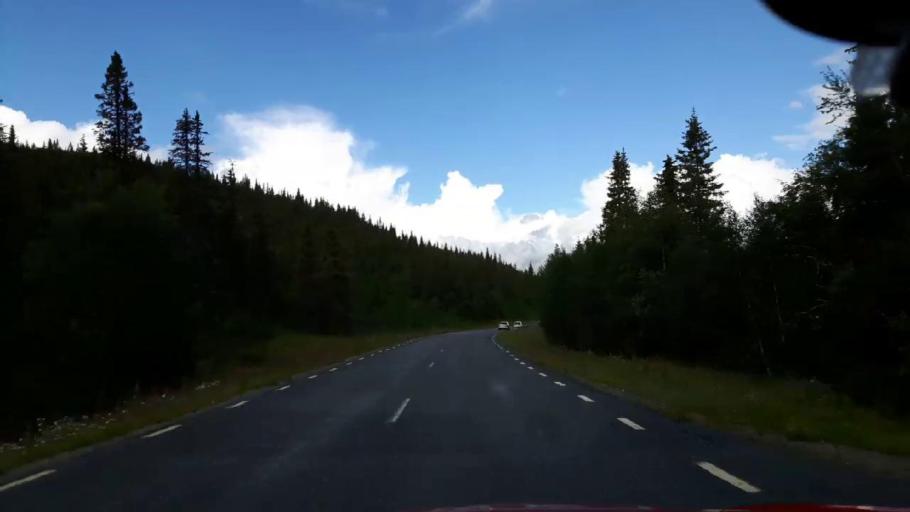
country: SE
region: Vaesterbotten
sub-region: Vilhelmina Kommun
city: Sjoberg
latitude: 65.0227
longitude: 15.1571
